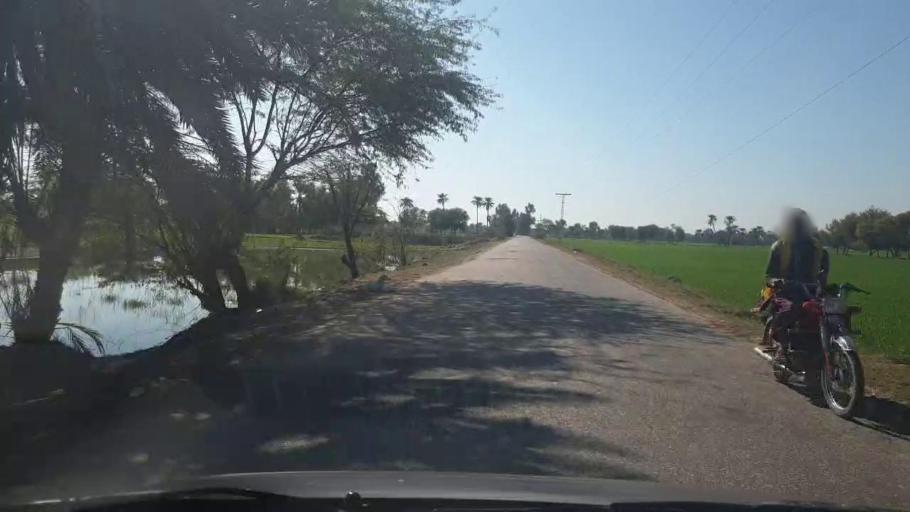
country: PK
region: Sindh
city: Bozdar
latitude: 27.1043
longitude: 68.6321
